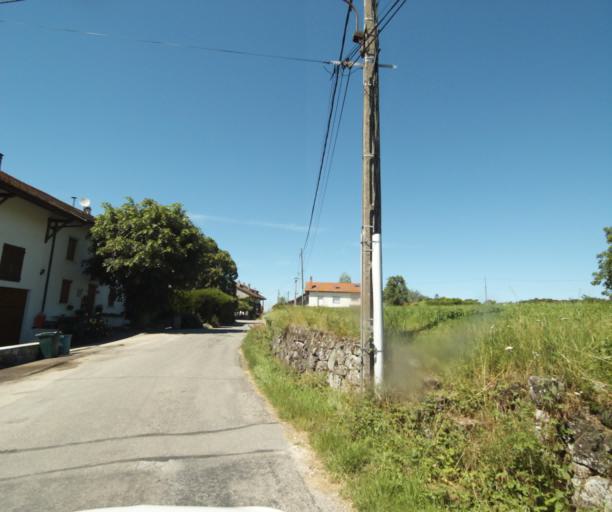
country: FR
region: Rhone-Alpes
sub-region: Departement de la Haute-Savoie
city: Ballaison
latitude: 46.2856
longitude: 6.3251
